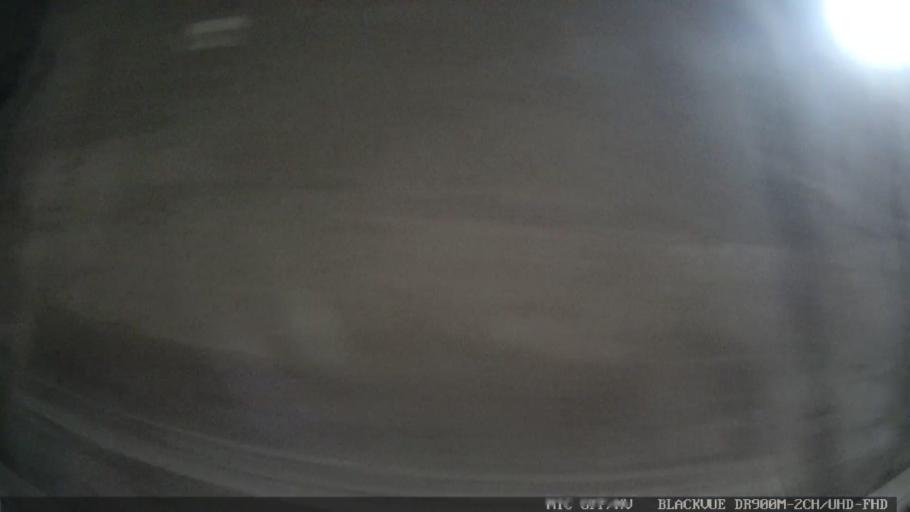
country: BR
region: Sao Paulo
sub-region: Cubatao
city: Cubatao
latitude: -23.9146
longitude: -46.5283
